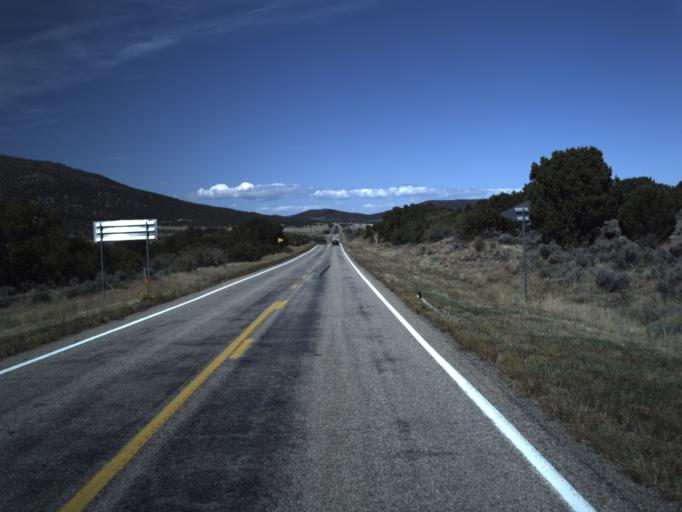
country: US
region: Utah
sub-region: Washington County
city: Enterprise
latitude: 37.4793
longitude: -113.6282
